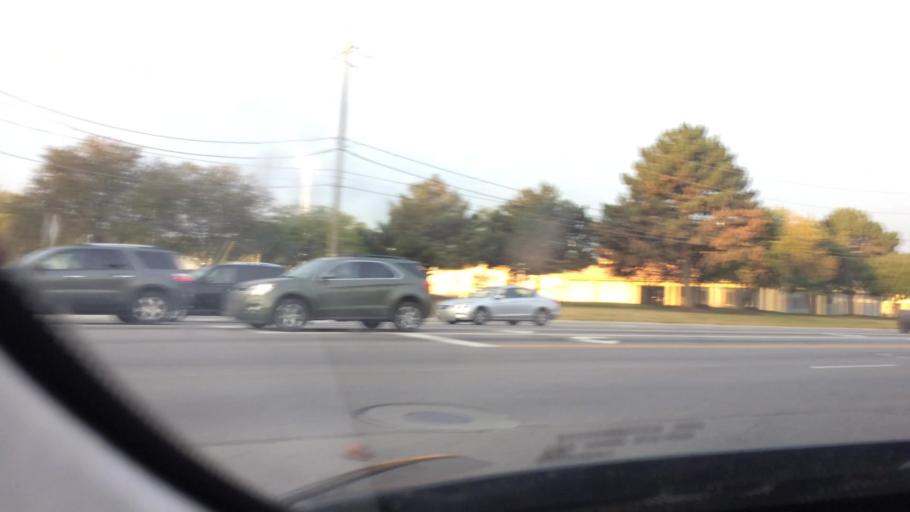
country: US
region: Ohio
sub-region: Lucas County
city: Holland
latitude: 41.6168
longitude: -83.6648
